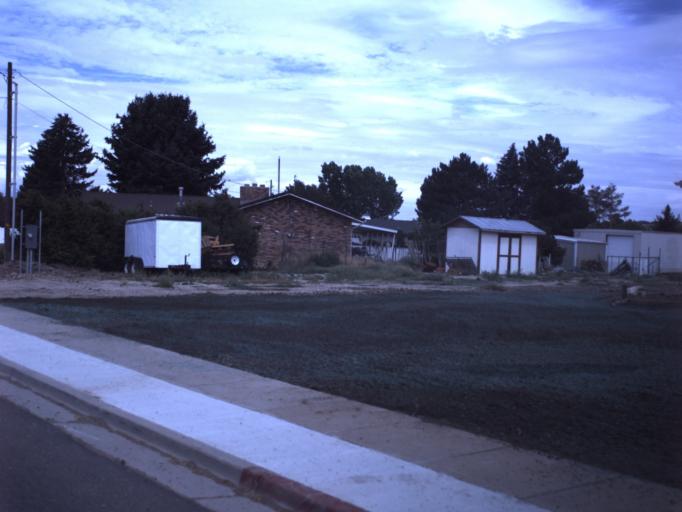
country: US
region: Utah
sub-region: Davis County
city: South Weber
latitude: 41.1346
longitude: -111.9498
